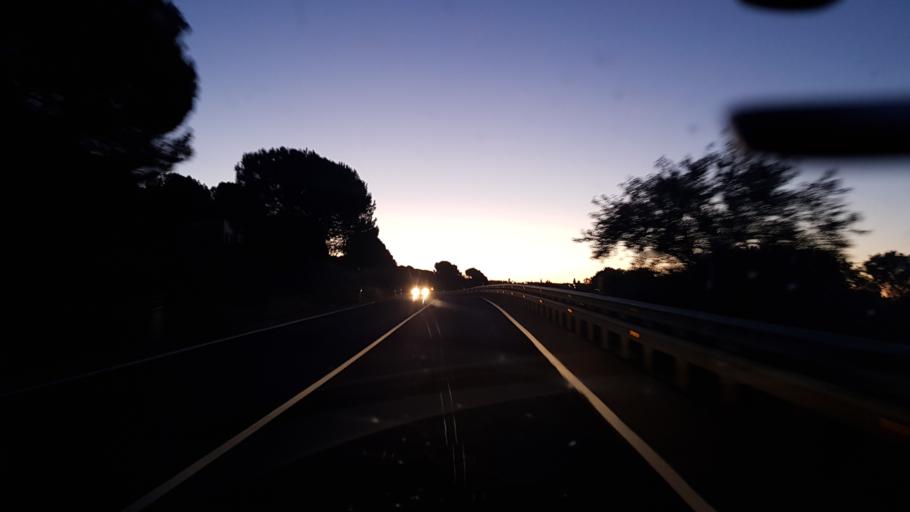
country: ES
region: Castille and Leon
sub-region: Provincia de Zamora
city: Toro
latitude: 41.5075
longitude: -5.4386
